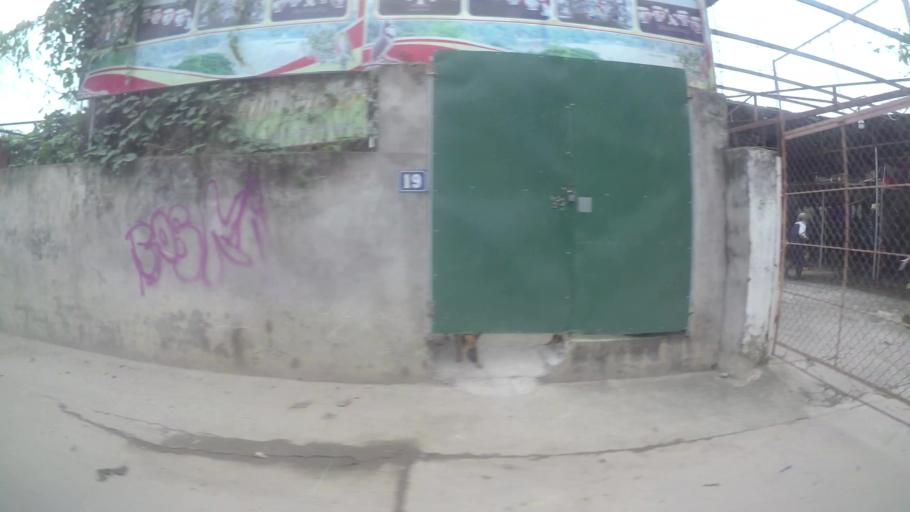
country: VN
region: Ha Noi
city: Tay Ho
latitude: 21.0662
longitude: 105.8358
